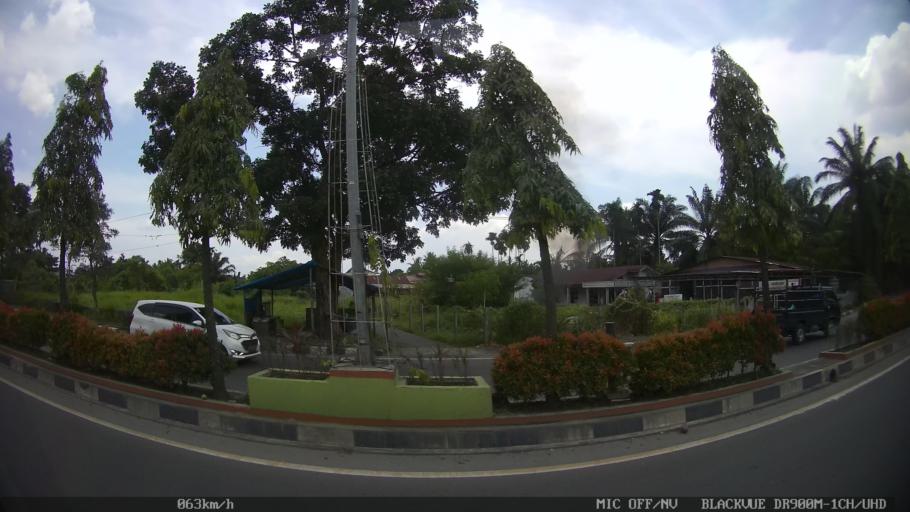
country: ID
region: North Sumatra
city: Binjai
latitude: 3.6041
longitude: 98.5328
